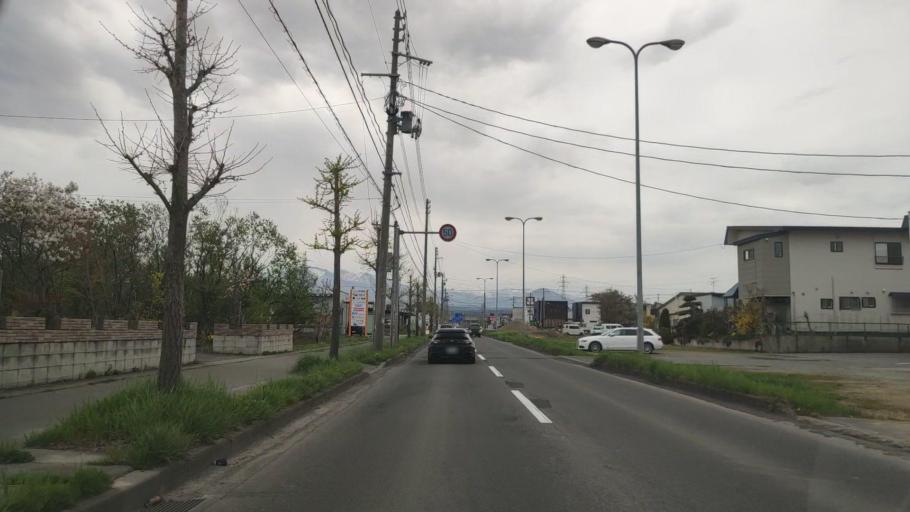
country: JP
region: Aomori
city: Aomori Shi
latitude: 40.8035
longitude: 140.7816
